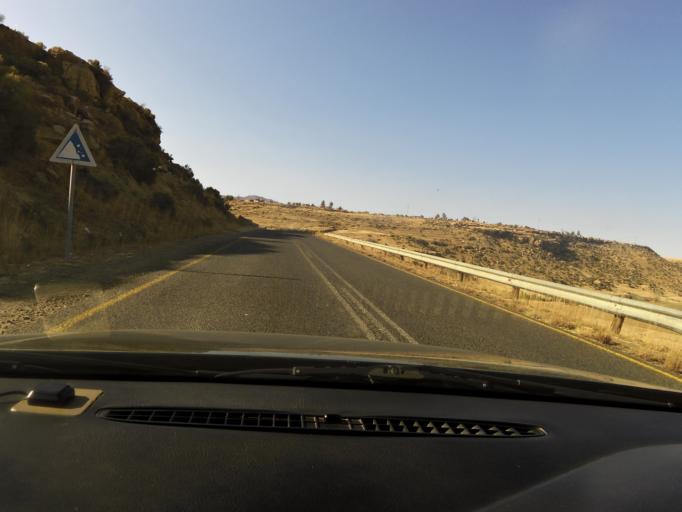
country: LS
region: Mohale's Hoek District
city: Mohale's Hoek
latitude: -30.0934
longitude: 27.4382
